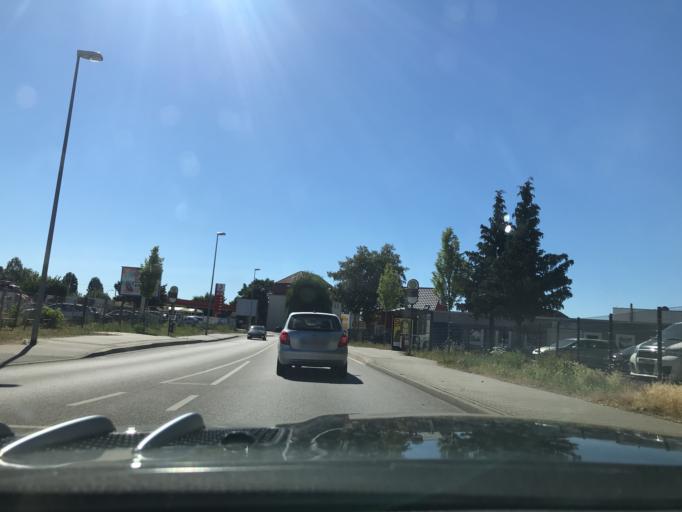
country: DE
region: Thuringia
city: Erfurt
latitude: 51.0102
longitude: 11.0163
